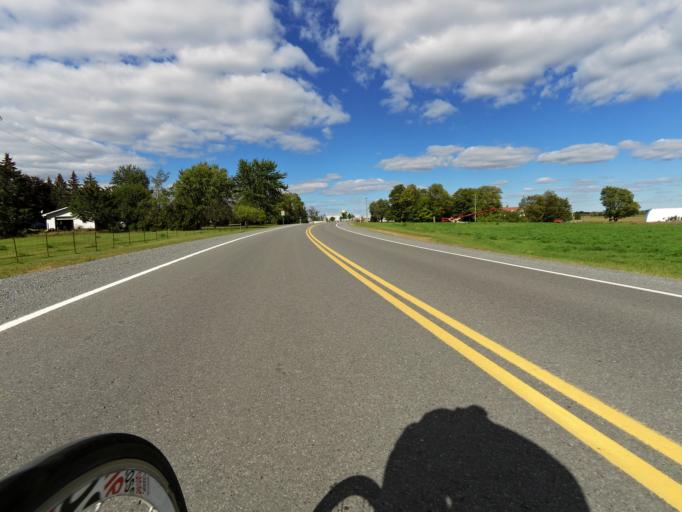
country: CA
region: Ontario
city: Bells Corners
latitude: 45.1744
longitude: -75.6623
